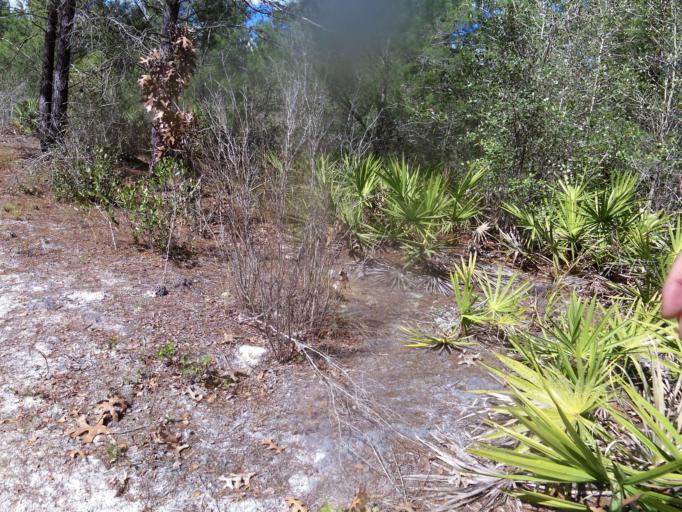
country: US
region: Florida
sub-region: Putnam County
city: Interlachen
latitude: 29.7625
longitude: -81.8529
